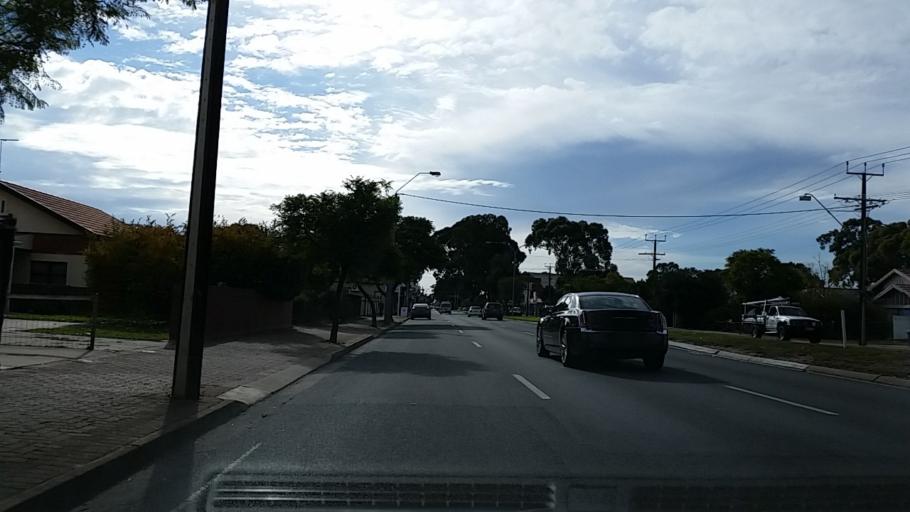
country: AU
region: South Australia
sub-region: Mitcham
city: Clapham
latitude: -34.9834
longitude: 138.5920
